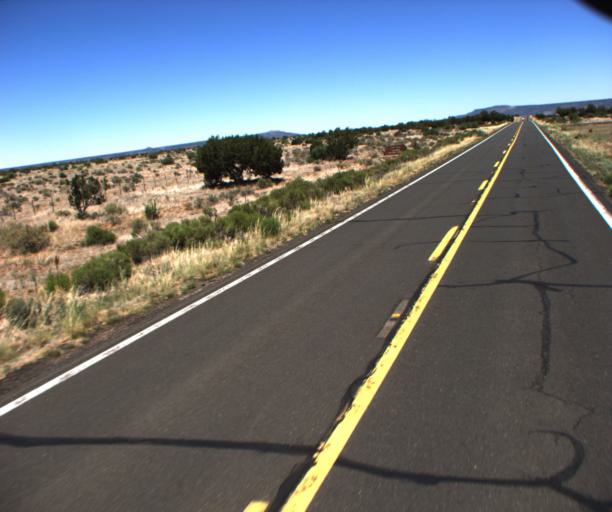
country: US
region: Arizona
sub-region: Coconino County
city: LeChee
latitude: 34.7584
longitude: -111.0256
